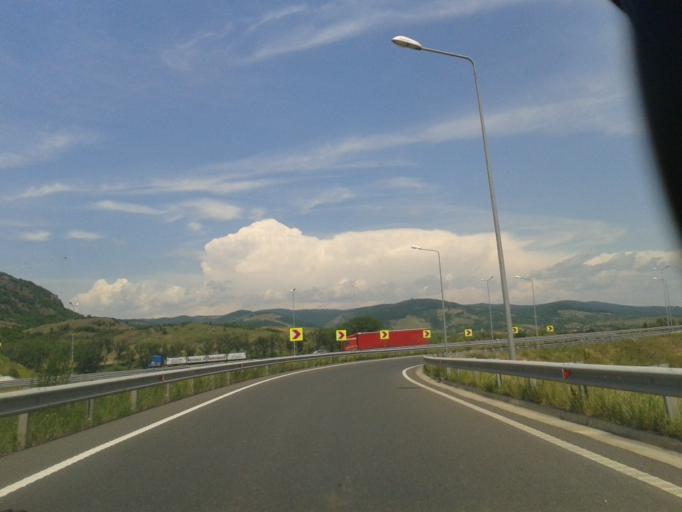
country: RO
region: Hunedoara
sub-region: Comuna Rapoltu Mare
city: Rapoltu Mare
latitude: 45.8486
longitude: 23.0457
